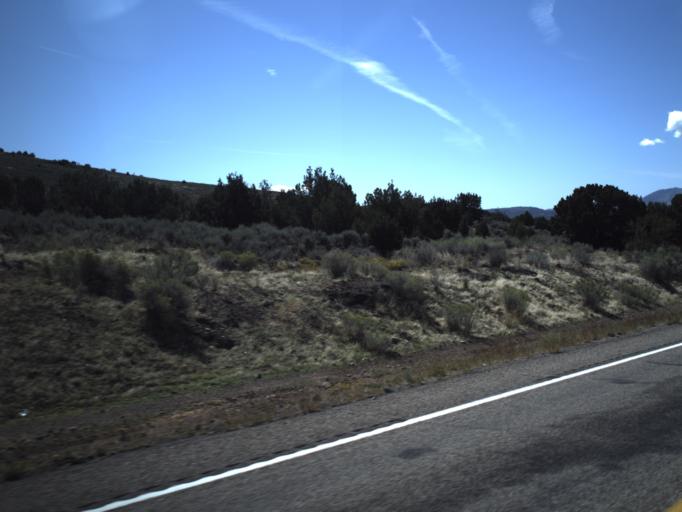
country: US
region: Utah
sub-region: Washington County
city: Ivins
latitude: 37.3593
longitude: -113.6750
